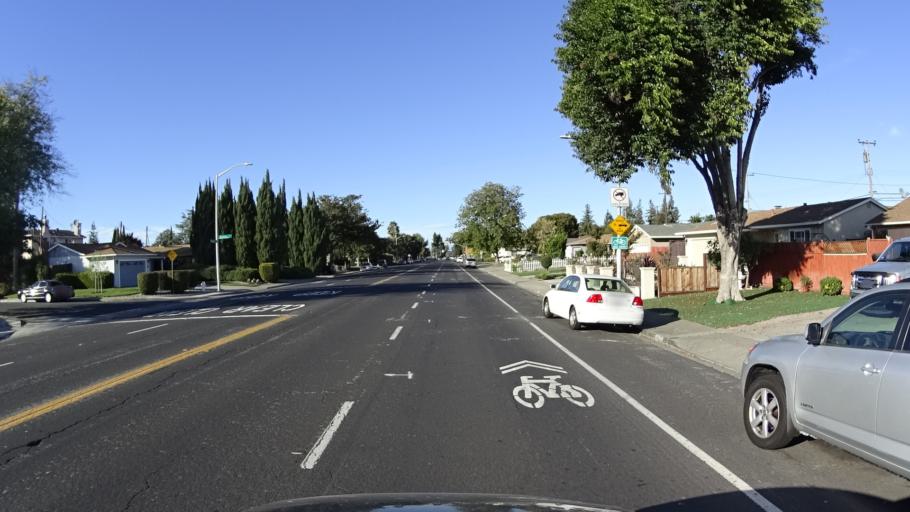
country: US
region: California
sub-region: Santa Clara County
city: Santa Clara
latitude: 37.3638
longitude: -121.9756
